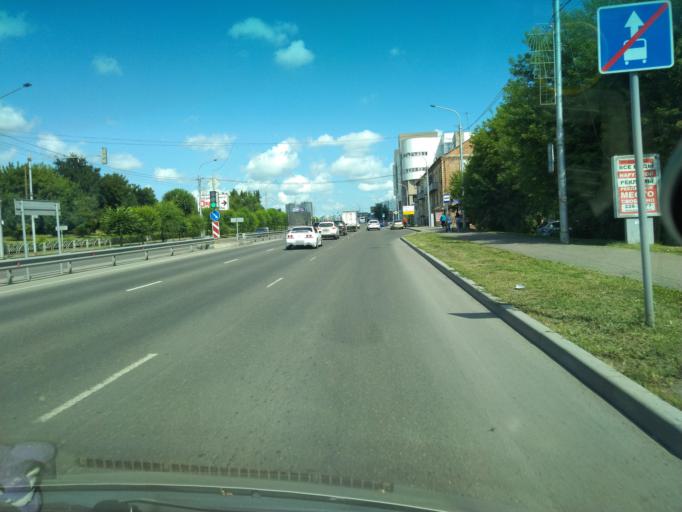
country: RU
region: Krasnoyarskiy
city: Krasnoyarsk
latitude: 56.0273
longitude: 92.8881
